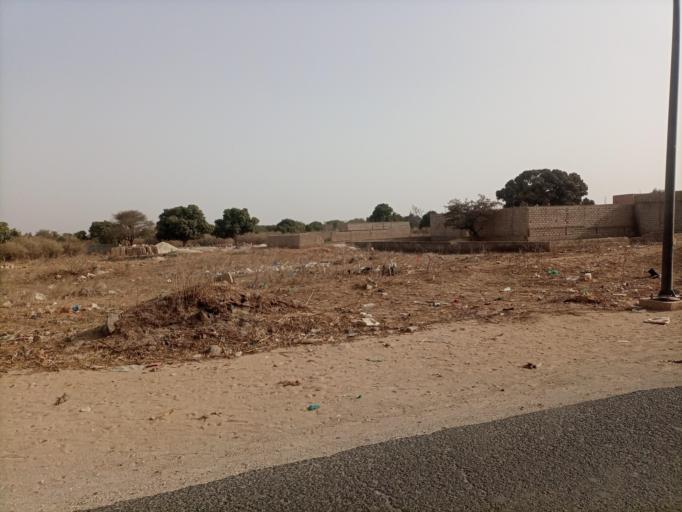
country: SN
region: Thies
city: Nguekhokh
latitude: 14.5847
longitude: -17.0302
